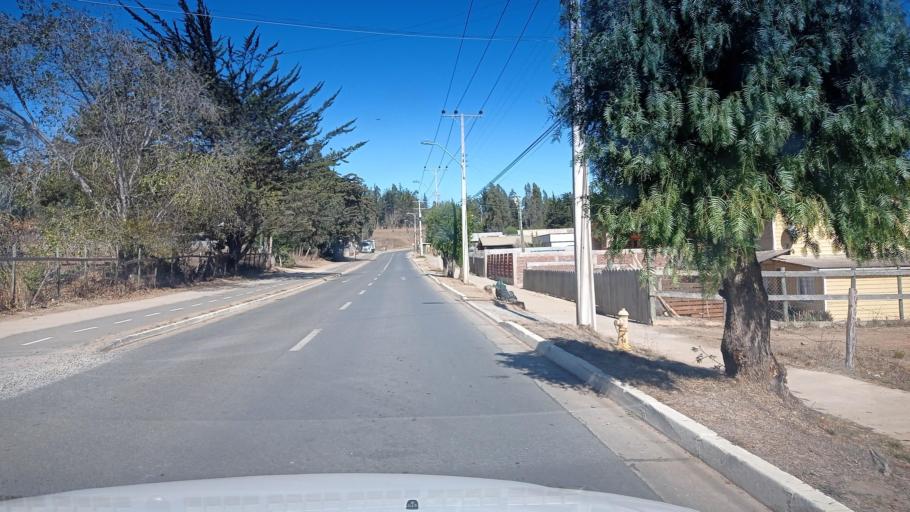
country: CL
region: O'Higgins
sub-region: Provincia de Colchagua
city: Santa Cruz
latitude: -34.4072
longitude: -71.9958
